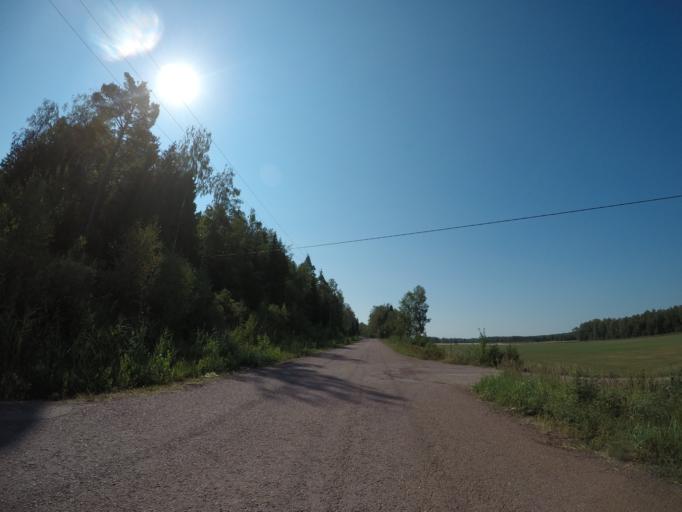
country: AX
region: Alands landsbygd
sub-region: Saltvik
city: Saltvik
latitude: 60.2256
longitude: 20.0103
